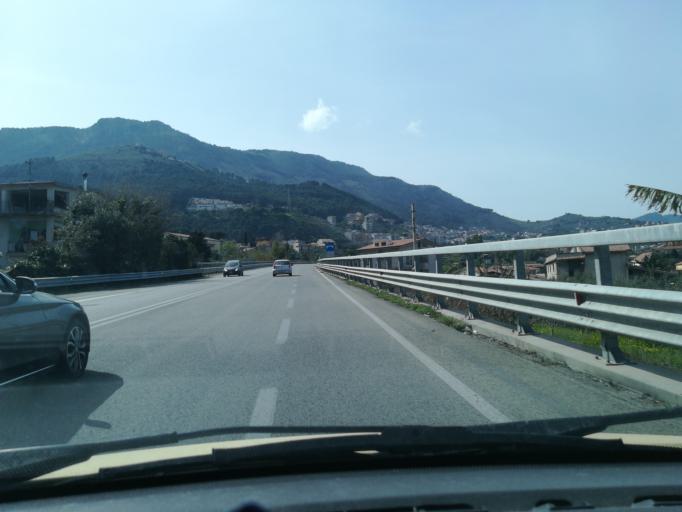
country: IT
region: Sicily
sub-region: Palermo
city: Piano Maglio-Blandino
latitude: 38.0557
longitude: 13.3103
